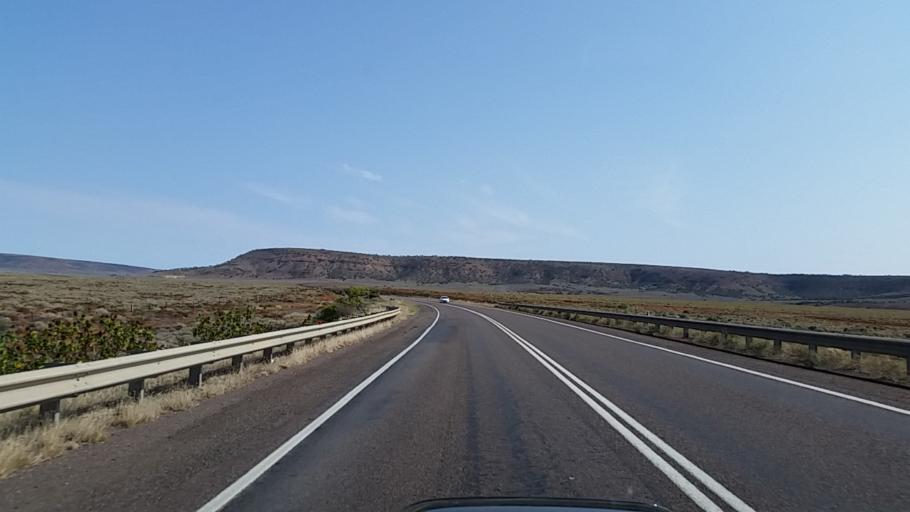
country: AU
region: South Australia
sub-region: Port Augusta
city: Port Augusta West
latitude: -32.5461
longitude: 137.6363
